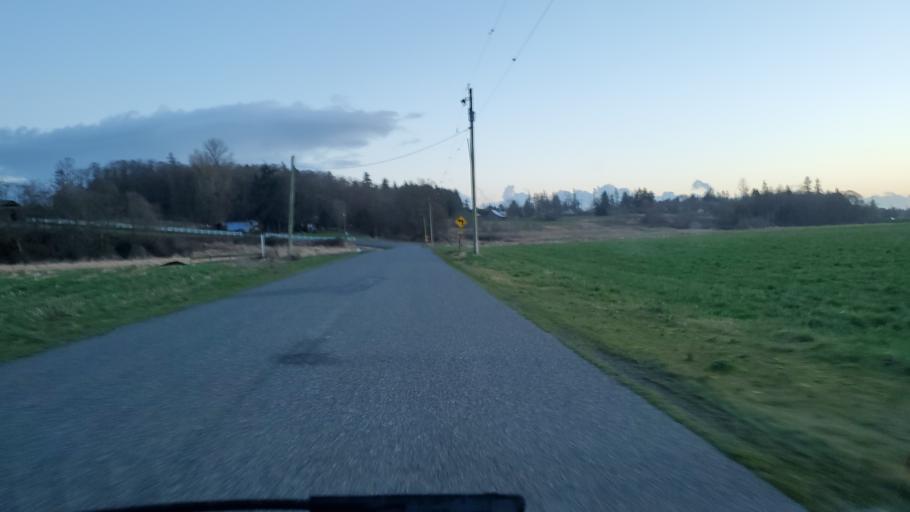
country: US
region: Washington
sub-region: Skagit County
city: Burlington
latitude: 48.4624
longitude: -122.2975
